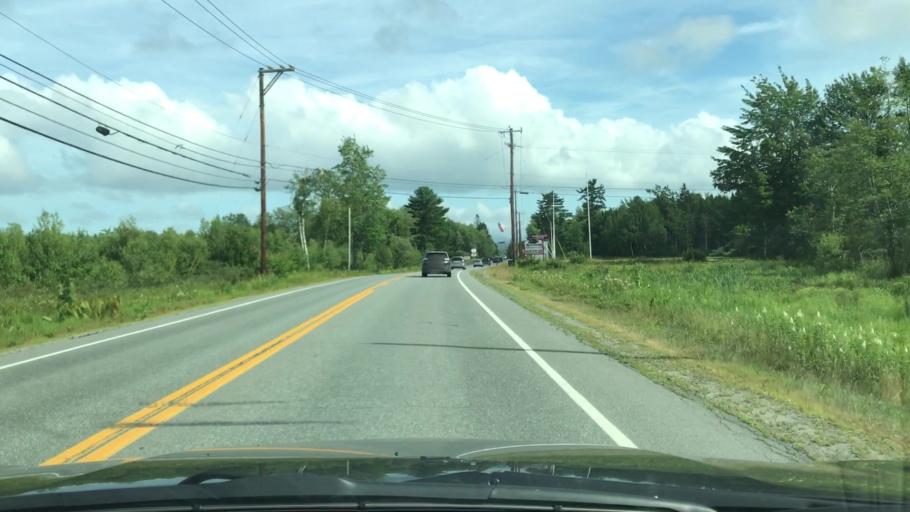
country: US
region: Maine
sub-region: Hancock County
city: Ellsworth
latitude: 44.5013
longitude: -68.3832
